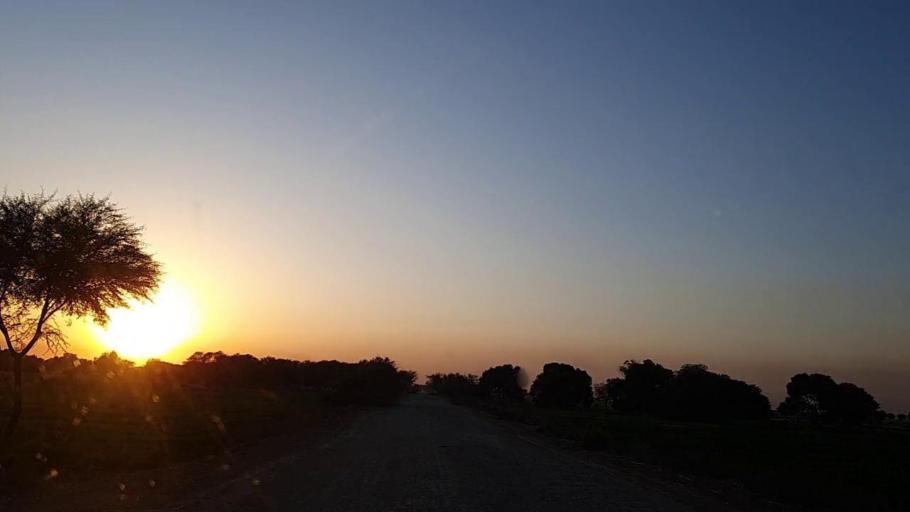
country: PK
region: Sindh
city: Daur
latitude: 26.3504
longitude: 68.3221
